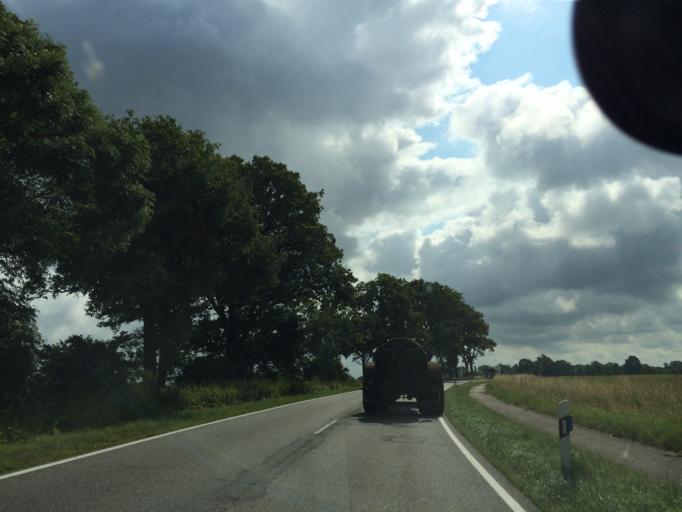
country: DE
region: Schleswig-Holstein
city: Lindau
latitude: 54.3993
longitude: 9.8903
